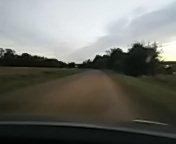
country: FR
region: Franche-Comte
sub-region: Departement du Doubs
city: Dannemarie-sur-Crete
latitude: 47.2151
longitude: 5.8464
